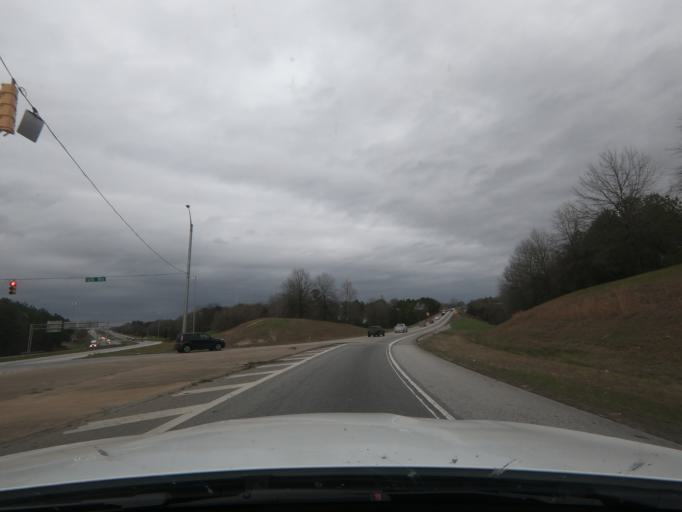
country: US
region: Alabama
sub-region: Russell County
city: Phenix City
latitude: 32.4864
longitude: -85.0321
